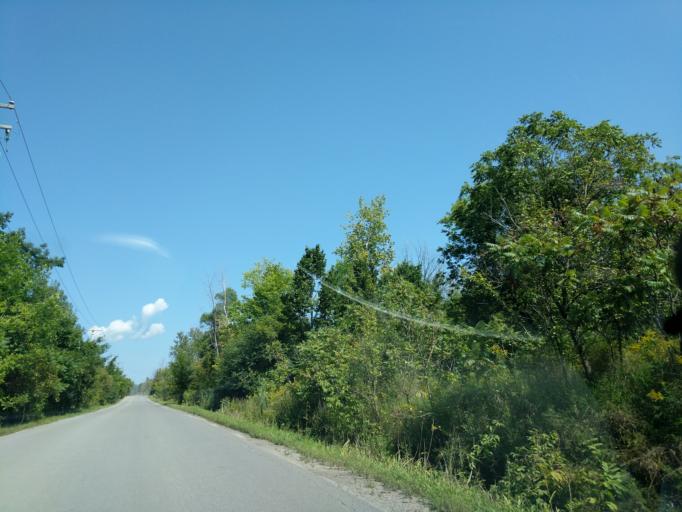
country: CA
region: Ontario
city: Bells Corners
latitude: 45.4335
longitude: -75.9009
